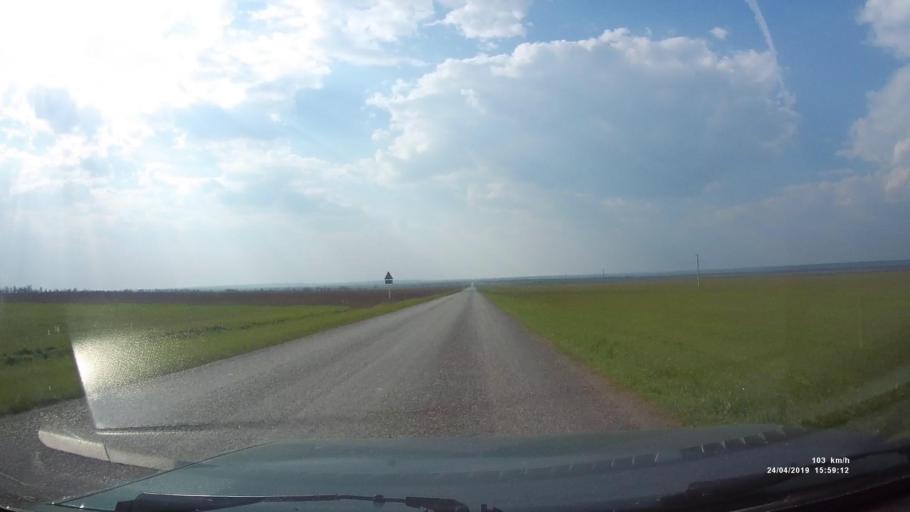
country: RU
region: Rostov
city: Sovetskoye
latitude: 46.6212
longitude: 42.4764
